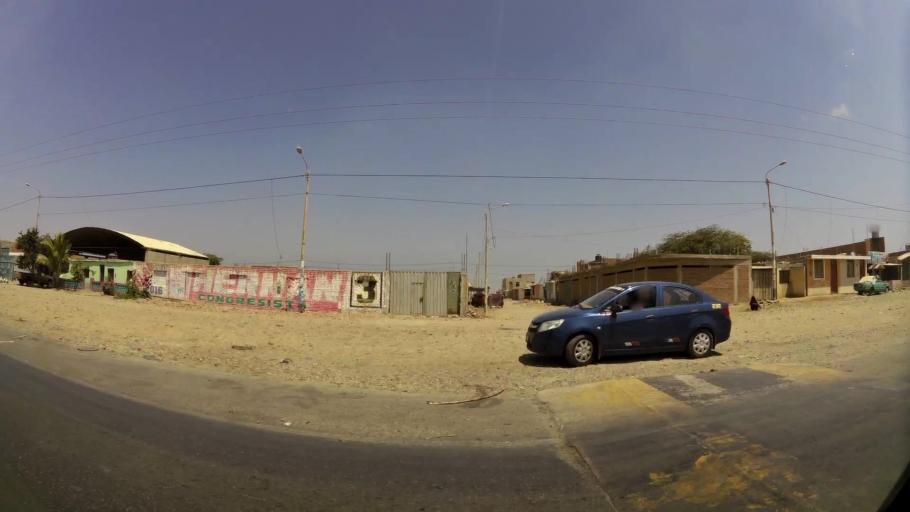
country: PE
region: La Libertad
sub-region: Provincia de Pacasmayo
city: Pacasmayo
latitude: -7.4185
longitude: -79.5452
